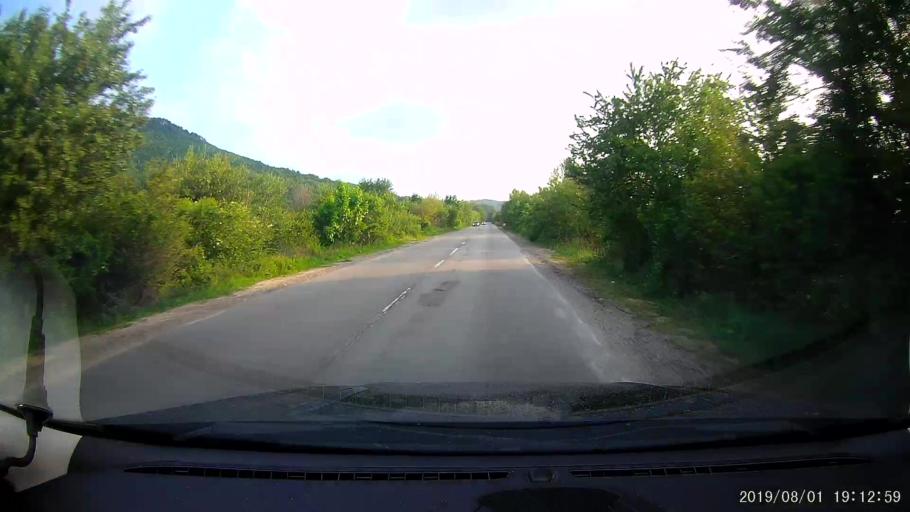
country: BG
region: Shumen
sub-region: Obshtina Smyadovo
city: Smyadovo
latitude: 42.9570
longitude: 26.9455
